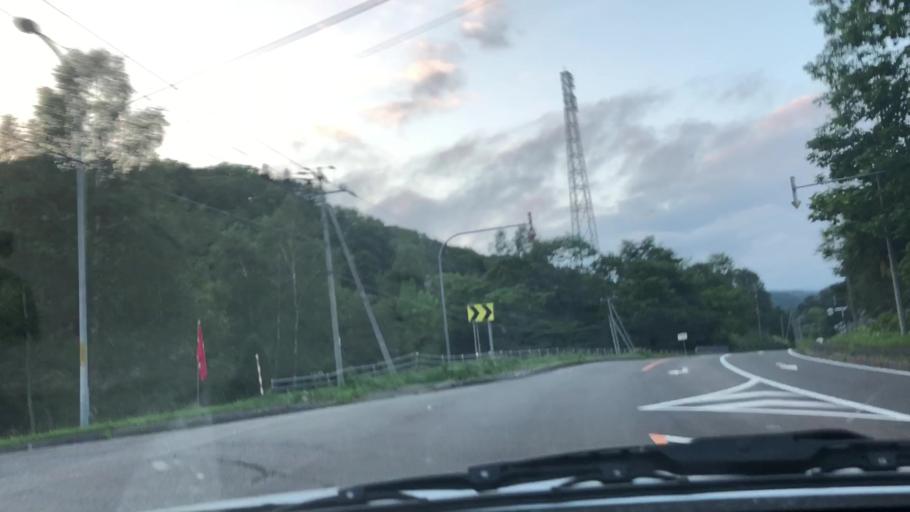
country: JP
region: Hokkaido
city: Chitose
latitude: 42.8729
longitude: 142.1309
